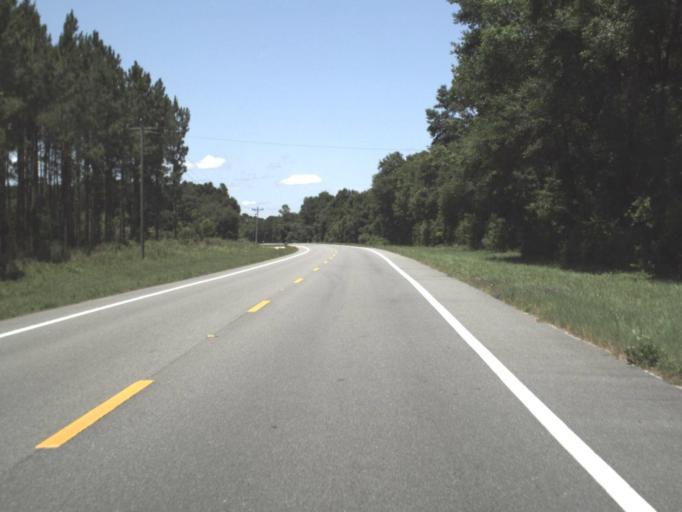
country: US
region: Florida
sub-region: Dixie County
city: Cross City
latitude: 29.8073
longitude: -82.9691
